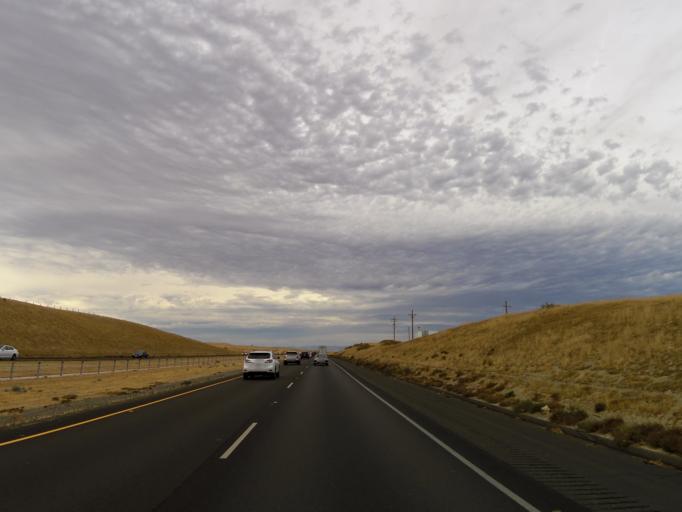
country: US
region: California
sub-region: Kings County
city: Kettleman City
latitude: 36.0424
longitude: -120.0440
